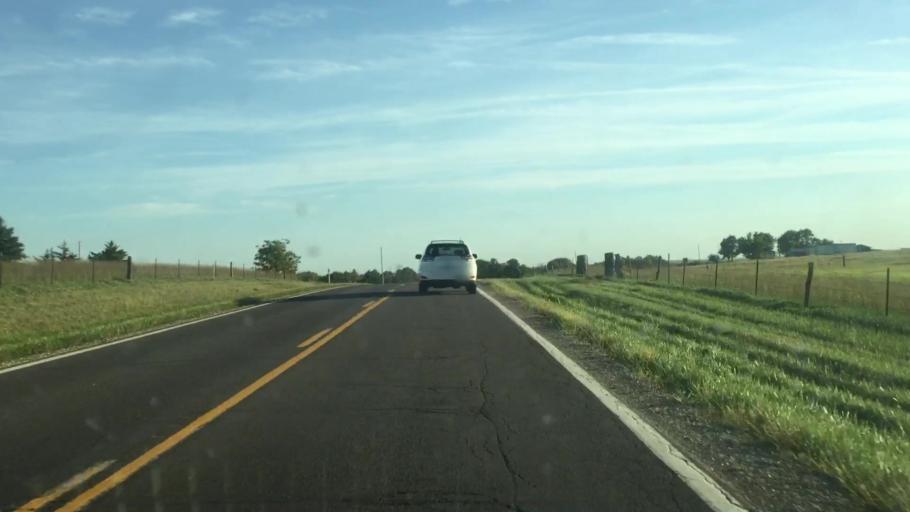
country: US
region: Kansas
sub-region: Brown County
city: Horton
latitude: 39.5622
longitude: -95.5247
